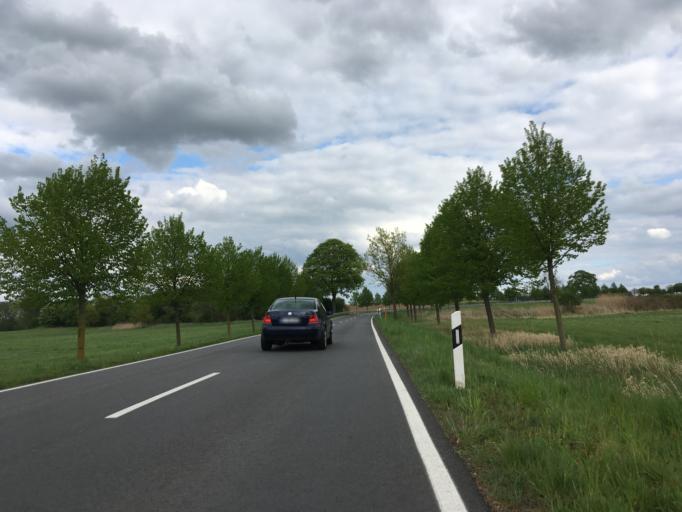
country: DE
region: Brandenburg
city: Bernau bei Berlin
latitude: 52.6611
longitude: 13.5955
